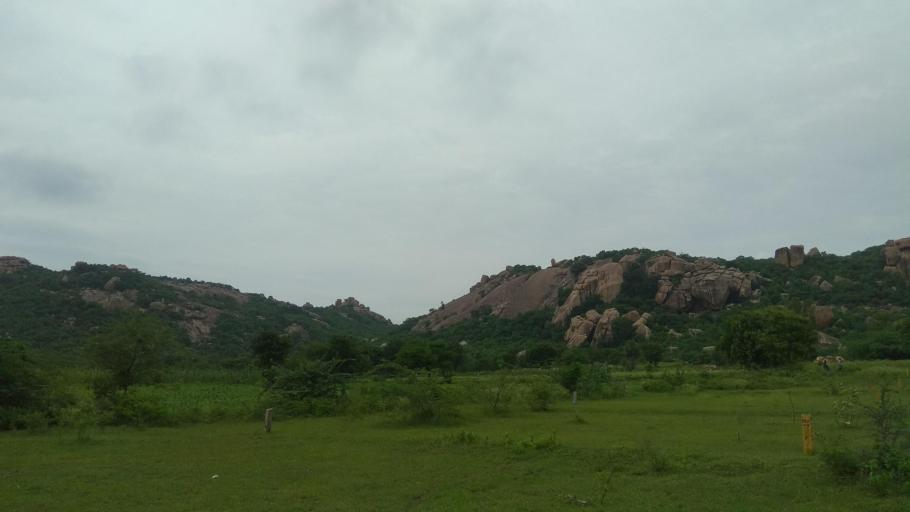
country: IN
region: Telangana
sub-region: Mahbubnagar
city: Farrukhnagar
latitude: 16.8857
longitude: 78.5142
